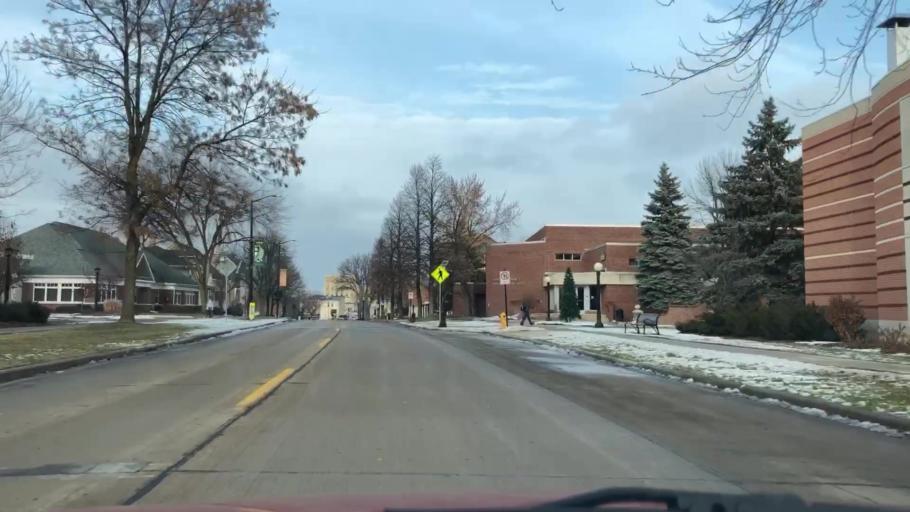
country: US
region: Wisconsin
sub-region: Brown County
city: De Pere
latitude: 44.4439
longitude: -88.0686
